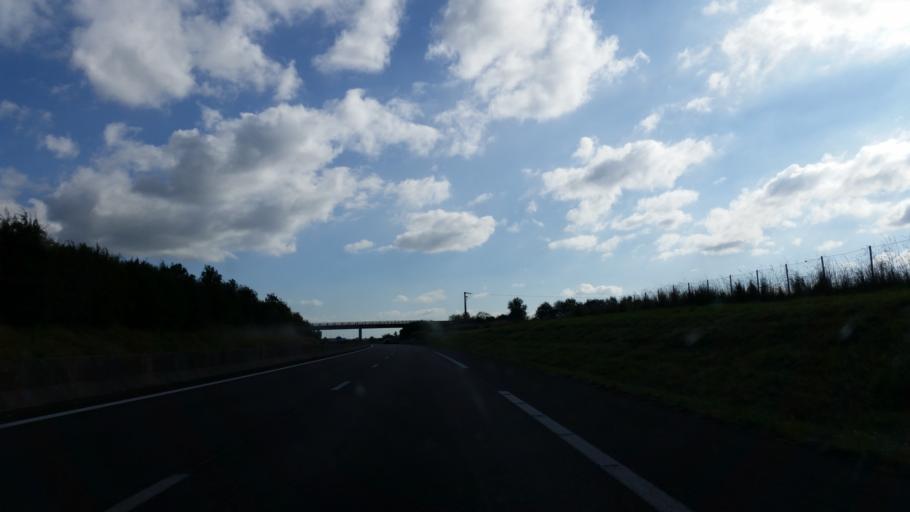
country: FR
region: Haute-Normandie
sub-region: Departement de la Seine-Maritime
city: Aumale
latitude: 49.7726
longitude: 1.7152
